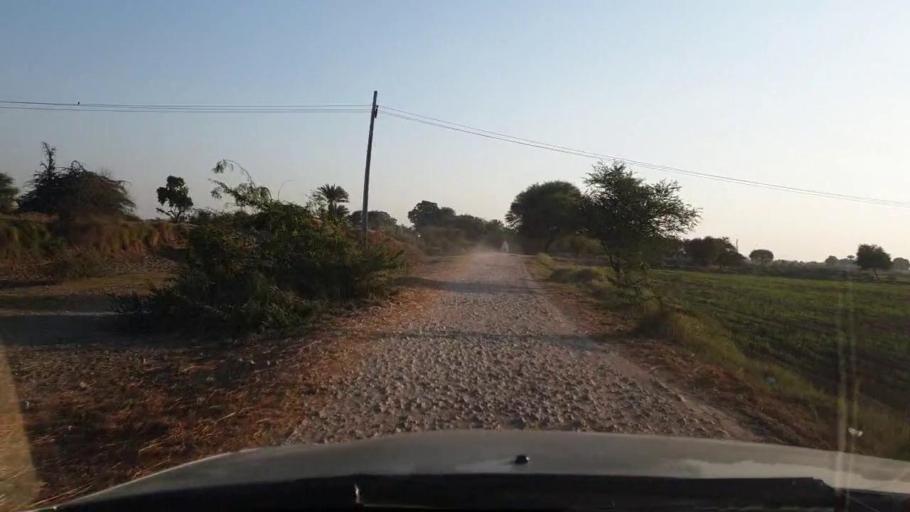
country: PK
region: Sindh
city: Matli
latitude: 25.0365
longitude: 68.6324
